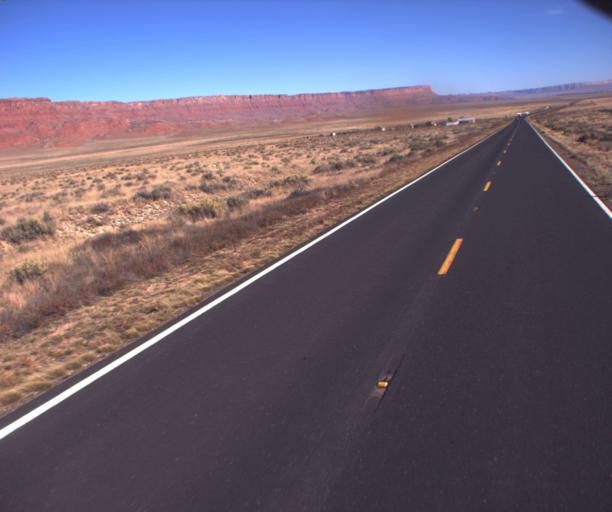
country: US
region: Arizona
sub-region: Coconino County
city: Fredonia
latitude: 36.7325
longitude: -112.0518
